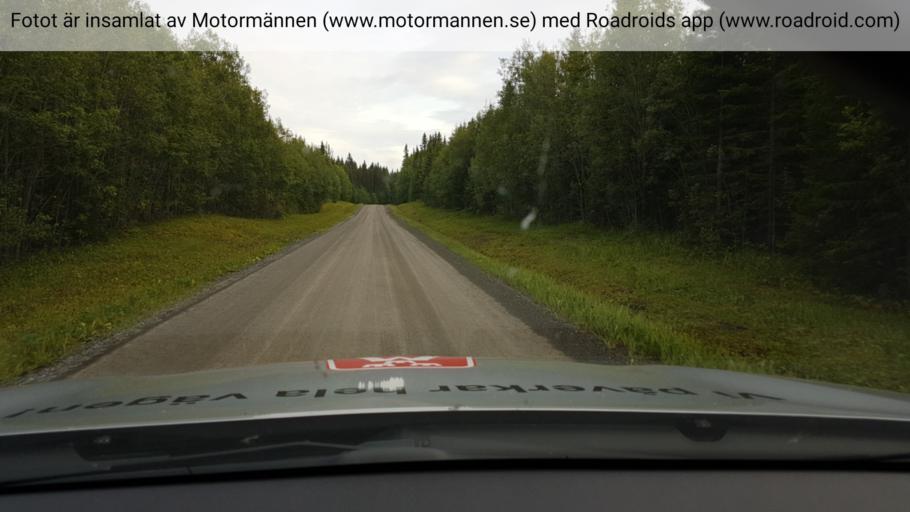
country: SE
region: Jaemtland
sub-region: OEstersunds Kommun
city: Lit
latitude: 63.6486
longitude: 14.9457
